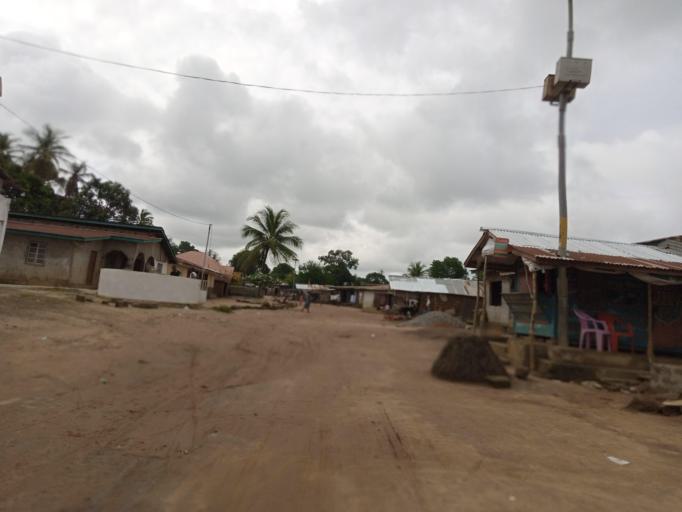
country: SL
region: Northern Province
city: Masoyila
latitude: 8.5888
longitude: -13.1989
